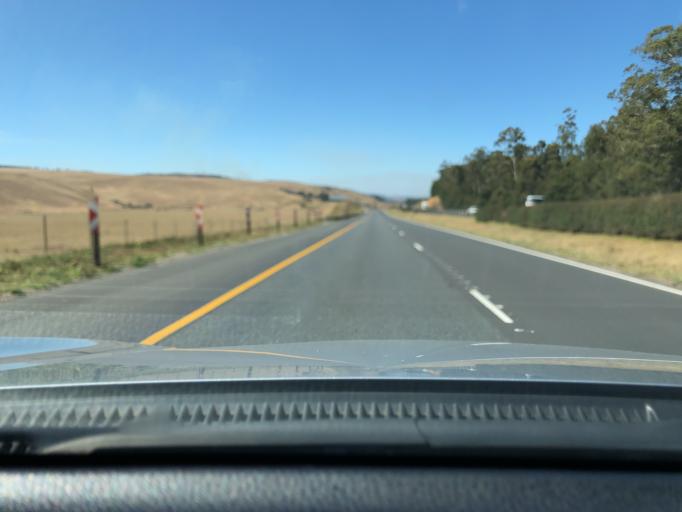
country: ZA
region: KwaZulu-Natal
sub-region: uMgungundlovu District Municipality
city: Mooirivier
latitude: -29.3255
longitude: 30.0539
